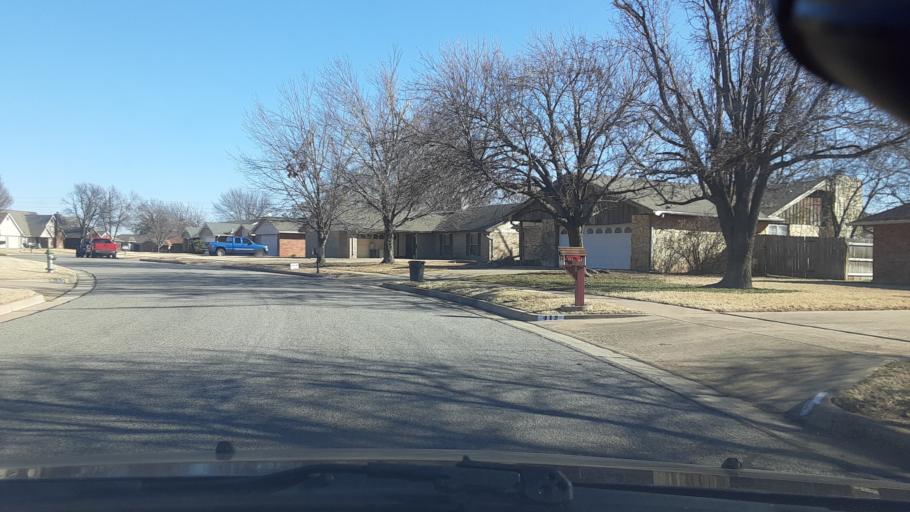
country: US
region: Oklahoma
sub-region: Kay County
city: Ponca City
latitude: 36.7294
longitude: -97.0877
